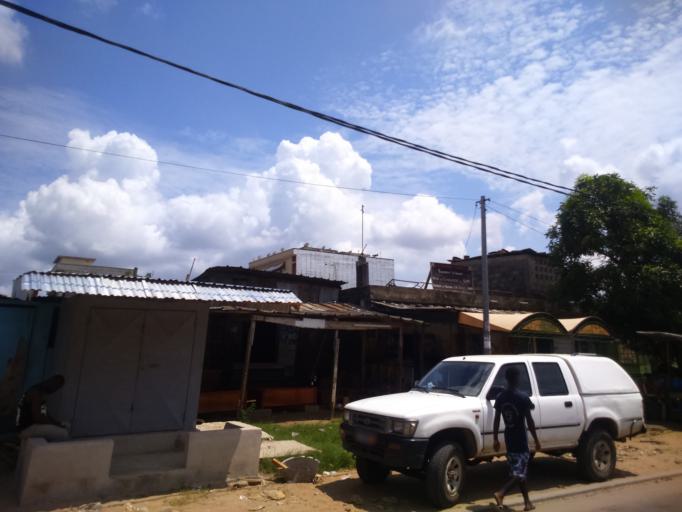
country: CI
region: Lagunes
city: Abidjan
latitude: 5.3433
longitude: -4.0875
